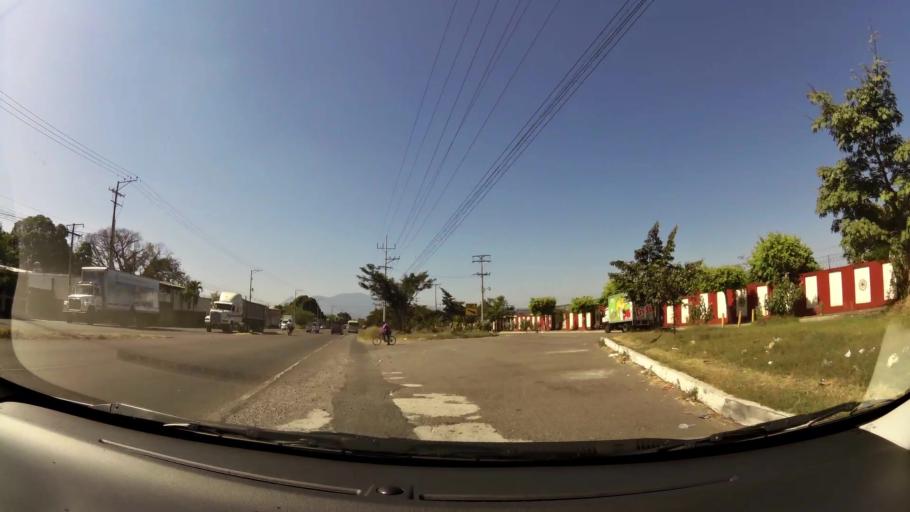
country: SV
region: La Libertad
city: Santa Tecla
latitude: 13.7285
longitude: -89.3797
